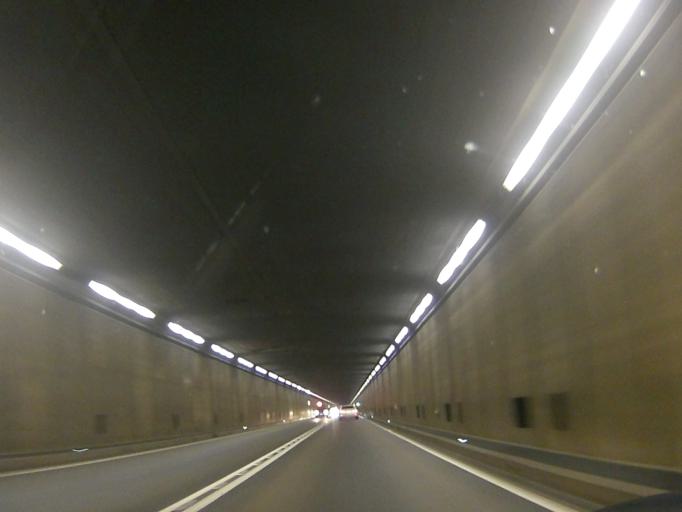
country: CH
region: Uri
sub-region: Uri
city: Andermatt
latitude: 46.5815
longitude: 8.5693
